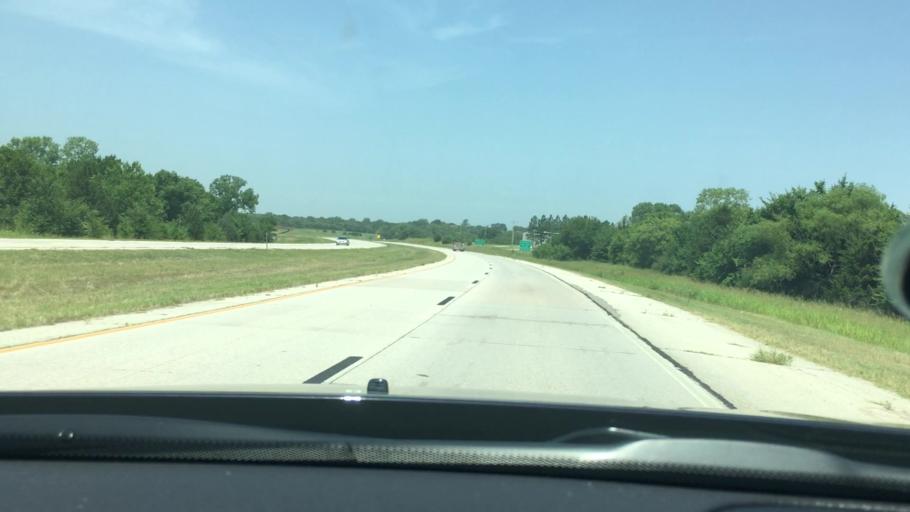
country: US
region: Oklahoma
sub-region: Pontotoc County
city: Ada
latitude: 34.7515
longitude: -96.6610
